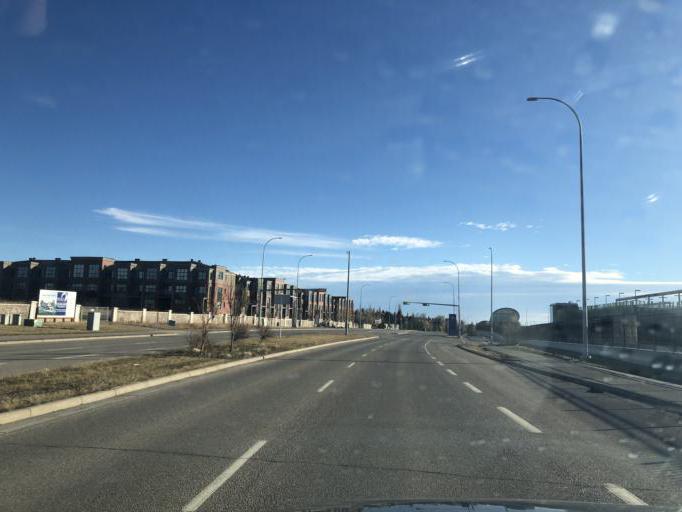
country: CA
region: Alberta
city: Calgary
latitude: 51.0378
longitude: -114.1922
